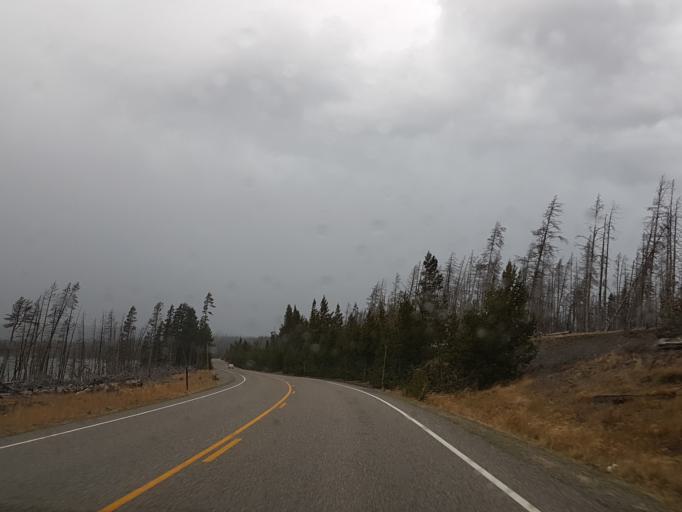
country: US
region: Montana
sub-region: Gallatin County
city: West Yellowstone
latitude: 44.4696
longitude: -110.5184
